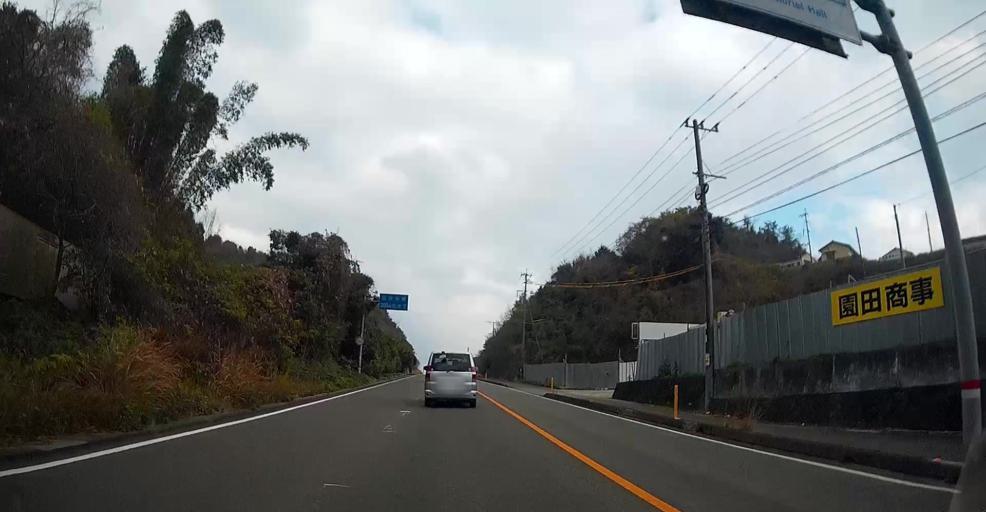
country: JP
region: Kumamoto
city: Yatsushiro
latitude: 32.5567
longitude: 130.4159
